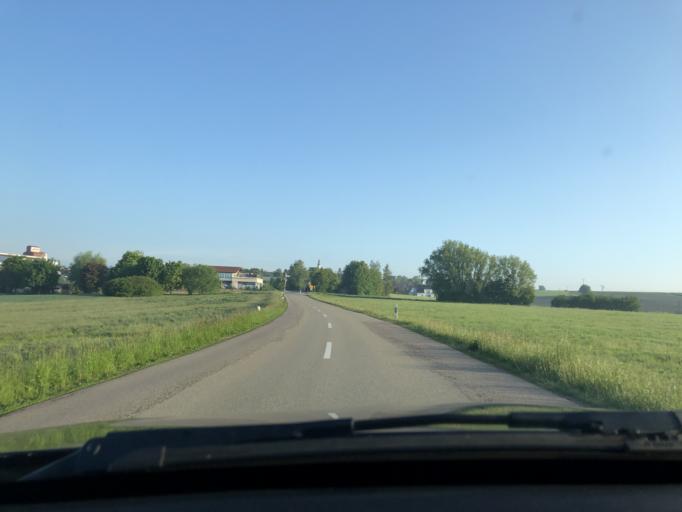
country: DE
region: Bavaria
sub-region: Upper Bavaria
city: Schweitenkirchen
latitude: 48.4986
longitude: 11.6118
